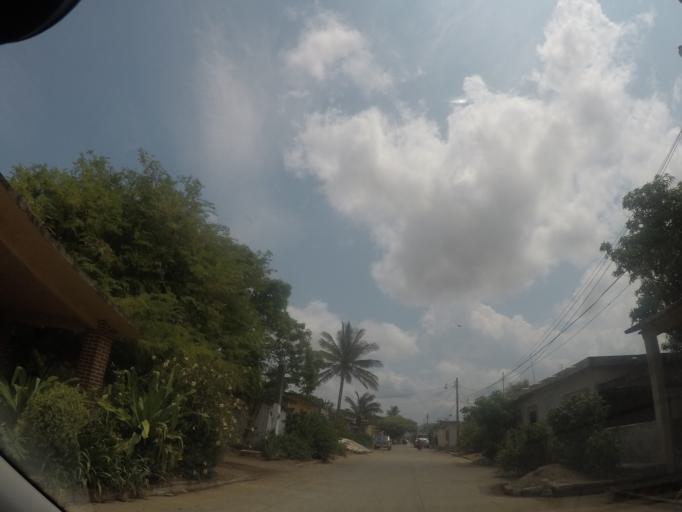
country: MX
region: Oaxaca
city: El Espinal
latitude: 16.5503
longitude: -94.9449
